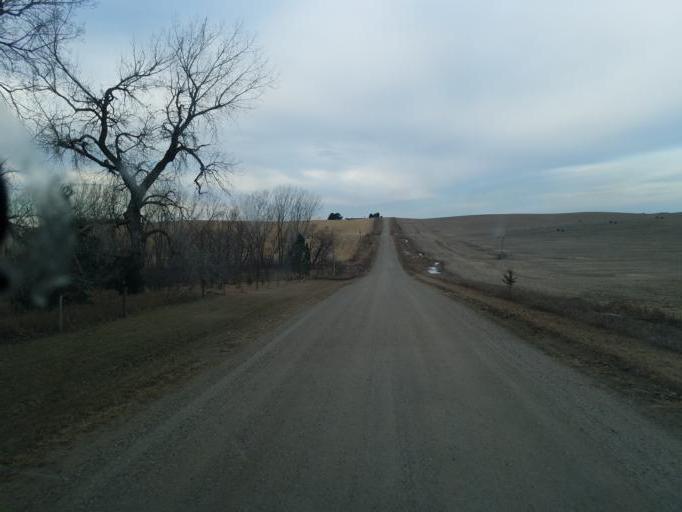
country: US
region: Nebraska
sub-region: Knox County
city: Bloomfield
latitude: 42.5833
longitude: -97.6311
